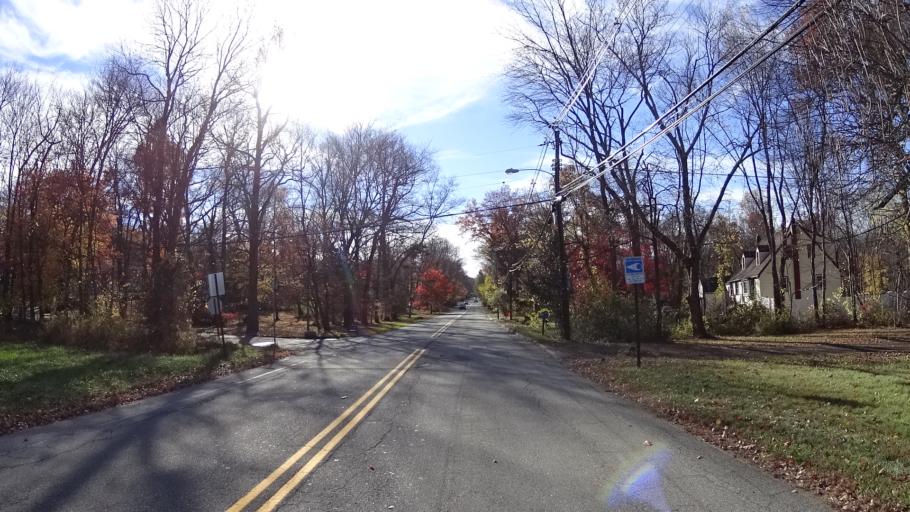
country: US
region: New Jersey
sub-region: Union County
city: Berkeley Heights
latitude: 40.6896
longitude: -74.4718
